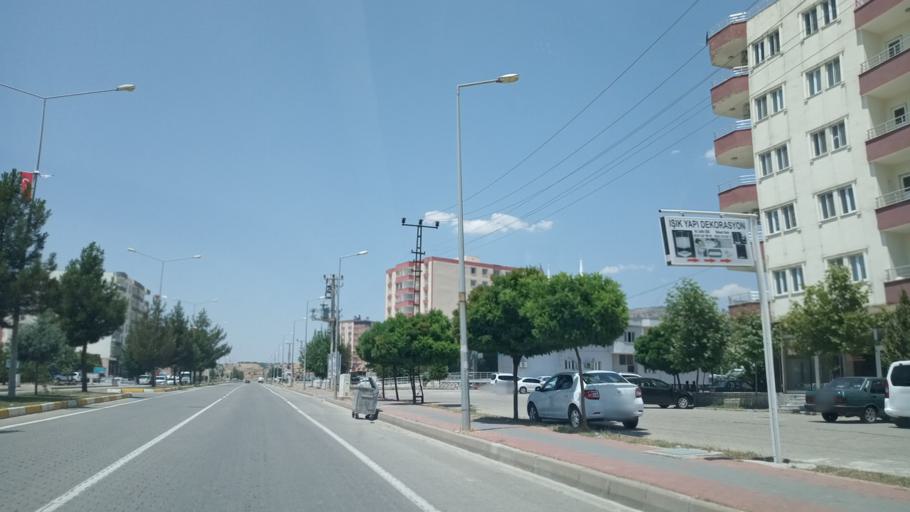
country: TR
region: Batman
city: Kozluk
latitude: 38.1673
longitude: 41.4955
